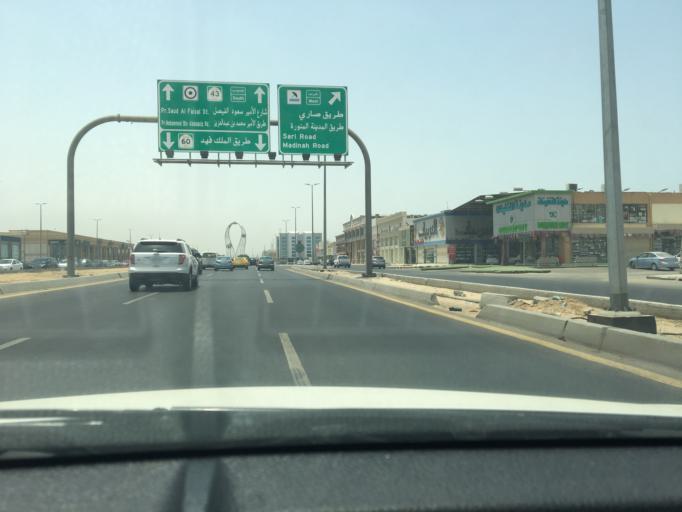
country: SA
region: Makkah
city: Jeddah
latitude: 21.5888
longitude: 39.1754
